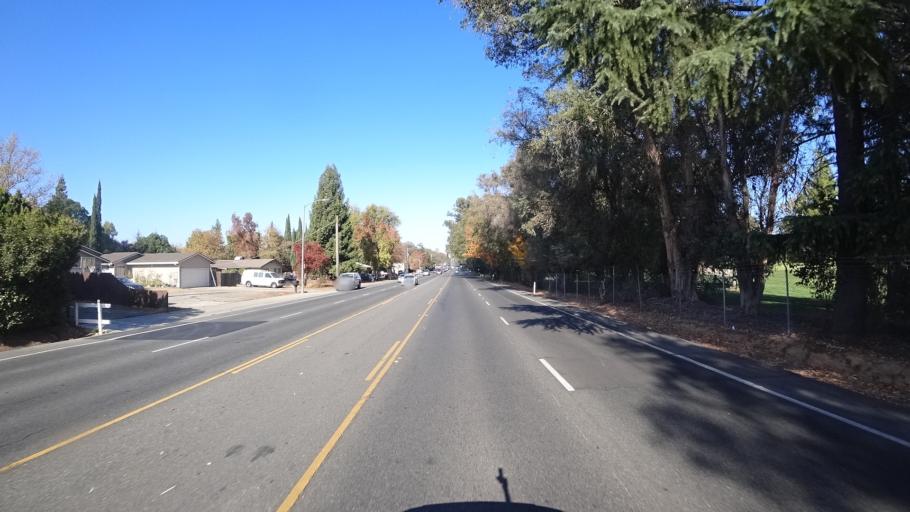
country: US
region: California
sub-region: Sacramento County
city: Fair Oaks
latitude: 38.6585
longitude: -121.2922
